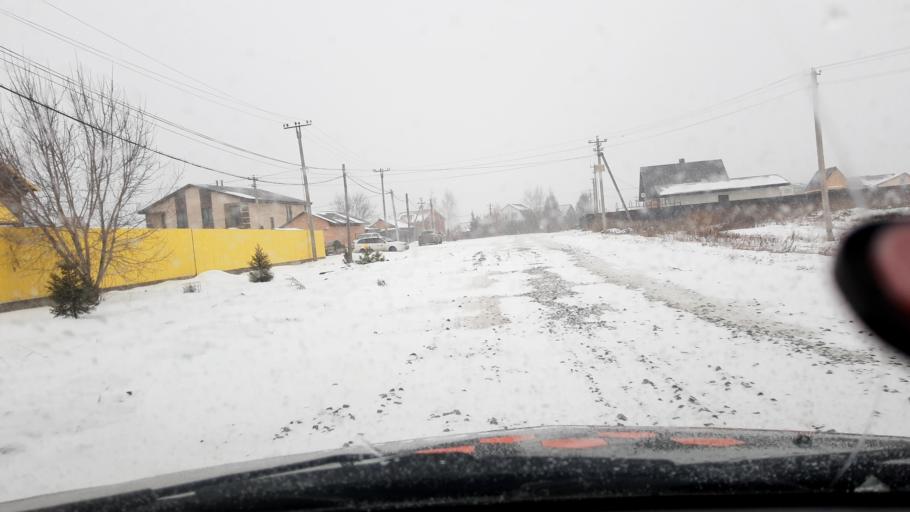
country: RU
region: Bashkortostan
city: Ufa
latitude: 54.5522
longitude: 55.9488
